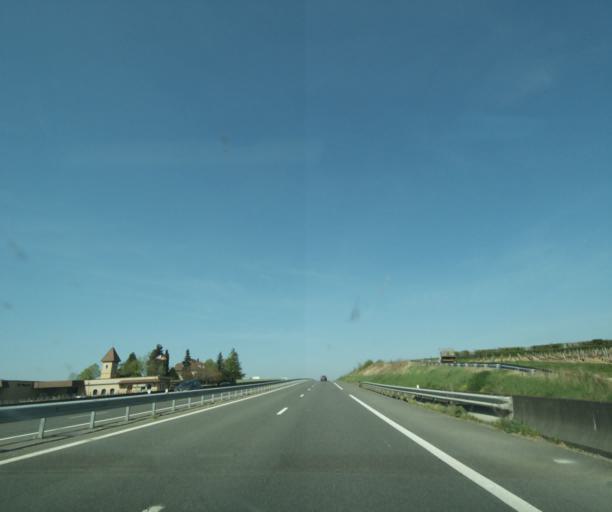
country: FR
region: Bourgogne
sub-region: Departement de la Nievre
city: Pouilly-sur-Loire
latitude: 47.3064
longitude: 2.9466
